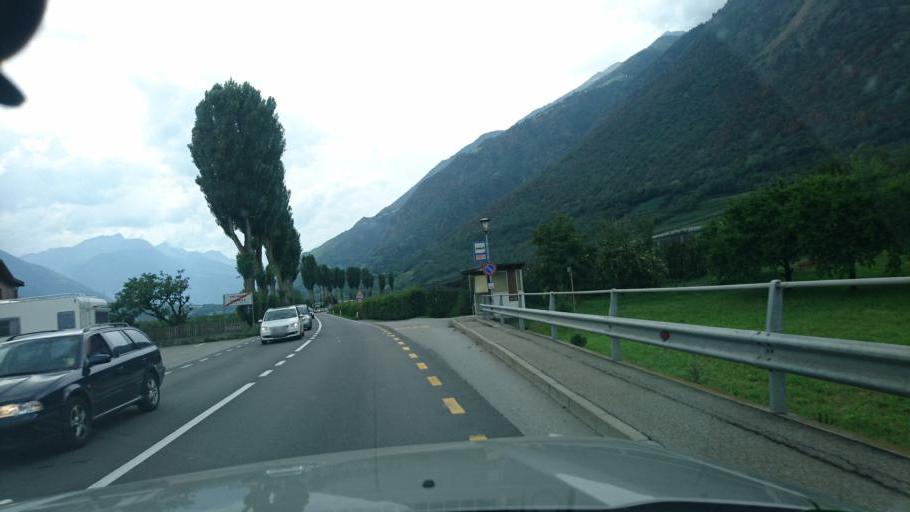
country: IT
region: Trentino-Alto Adige
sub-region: Bolzano
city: Castelbello
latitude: 46.6356
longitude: 10.9376
